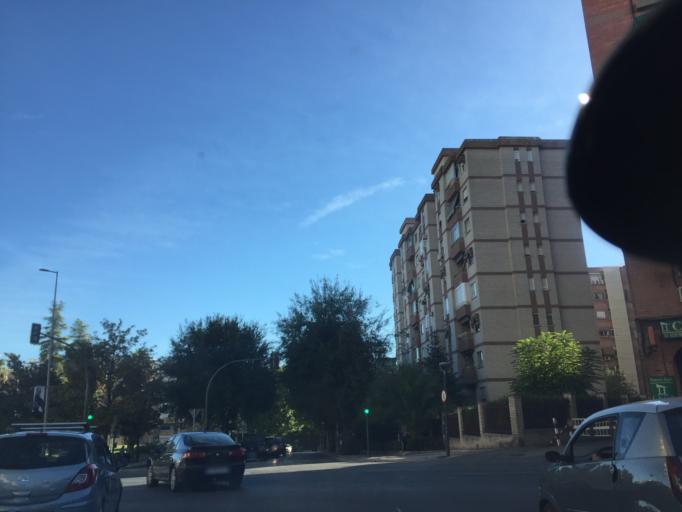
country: ES
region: Andalusia
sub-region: Provincia de Jaen
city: Jaen
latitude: 37.7784
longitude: -3.7854
